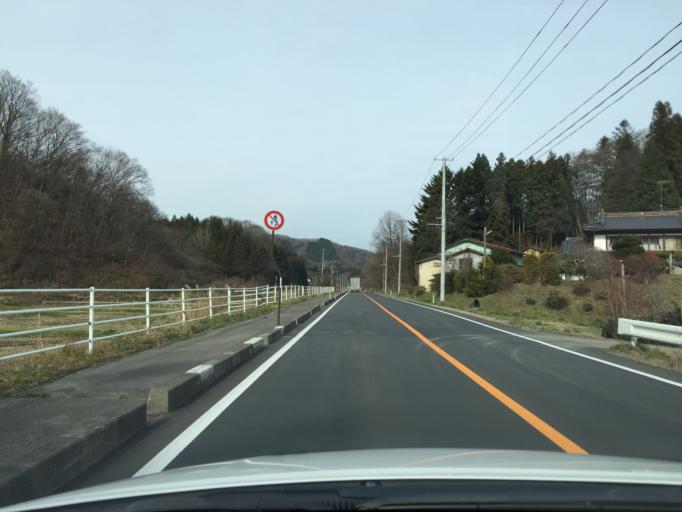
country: JP
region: Fukushima
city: Funehikimachi-funehiki
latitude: 37.3308
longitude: 140.6117
